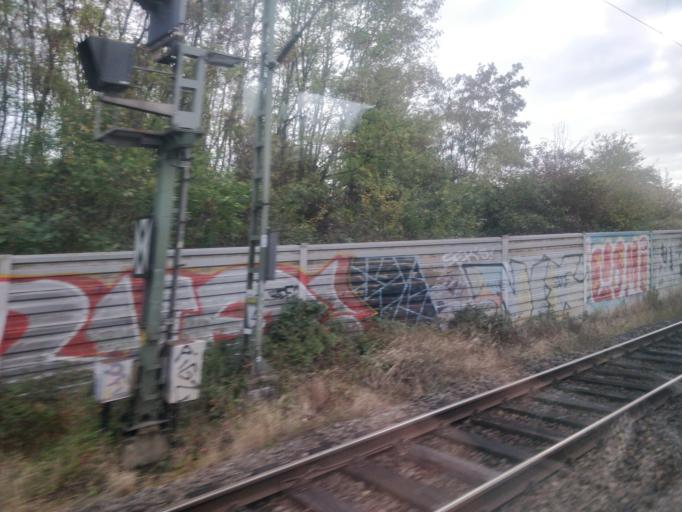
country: DE
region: North Rhine-Westphalia
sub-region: Regierungsbezirk Koln
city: Porz am Rhein
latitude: 50.8755
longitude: 7.0691
